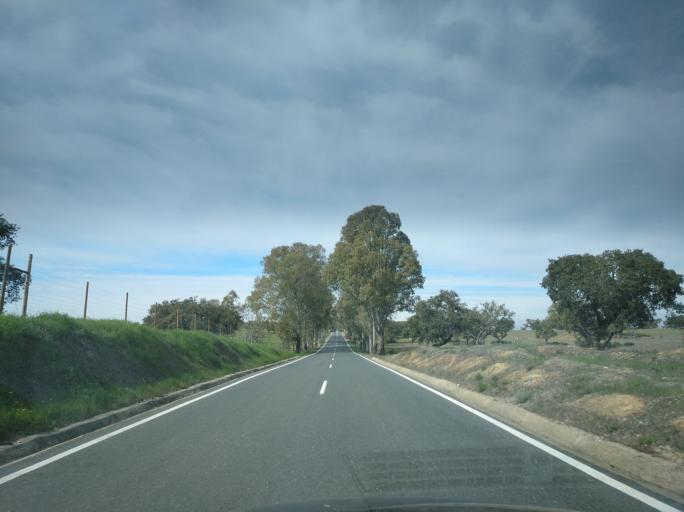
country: PT
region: Beja
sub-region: Mertola
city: Mertola
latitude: 37.7300
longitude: -7.7672
